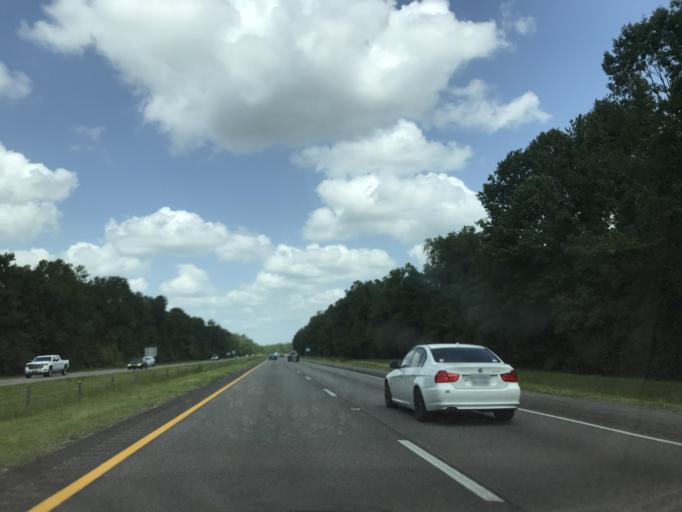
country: US
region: North Carolina
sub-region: Pender County
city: Rocky Point
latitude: 34.4535
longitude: -77.8778
